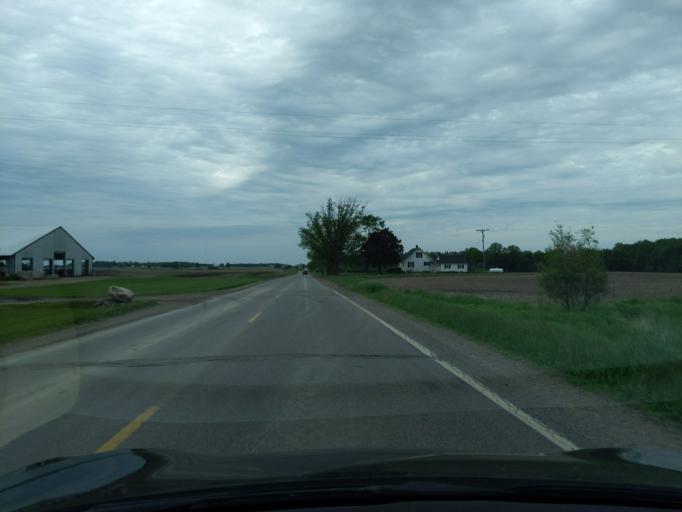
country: US
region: Michigan
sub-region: Ingham County
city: Mason
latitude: 42.6347
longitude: -84.3639
